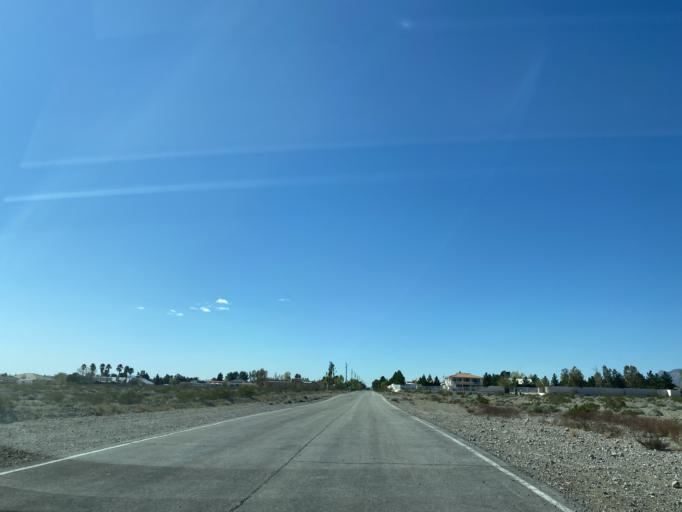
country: US
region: Nevada
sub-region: Clark County
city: North Las Vegas
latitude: 36.3354
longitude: -115.2829
